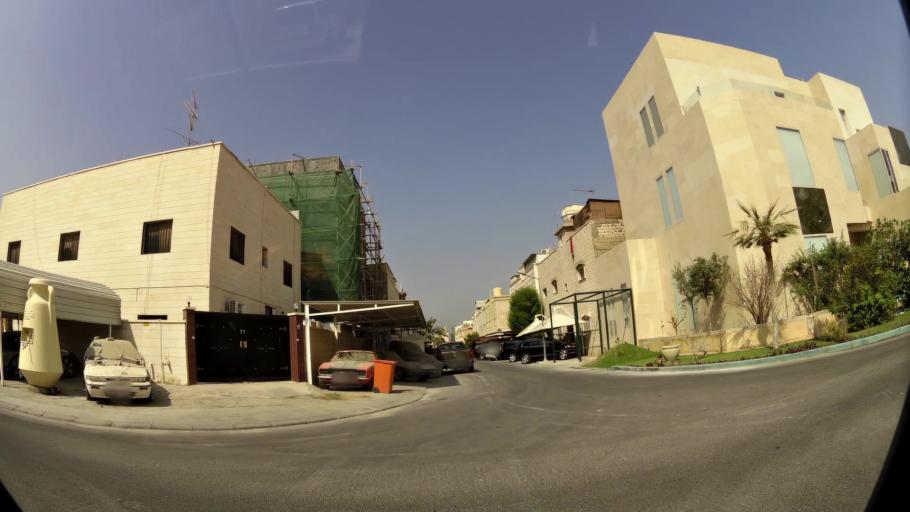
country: KW
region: Al Asimah
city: Ad Dasmah
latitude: 29.3455
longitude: 48.0070
